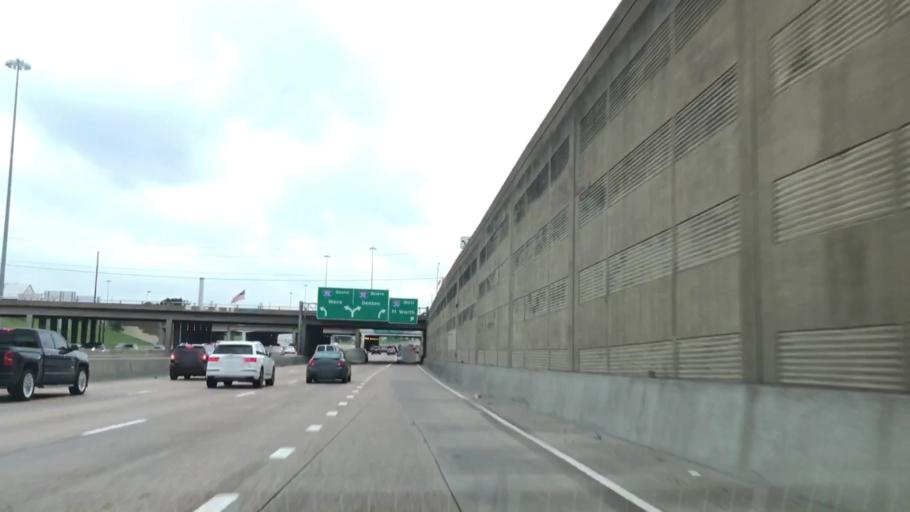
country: US
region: Texas
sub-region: Dallas County
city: Dallas
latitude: 32.7722
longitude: -96.7998
